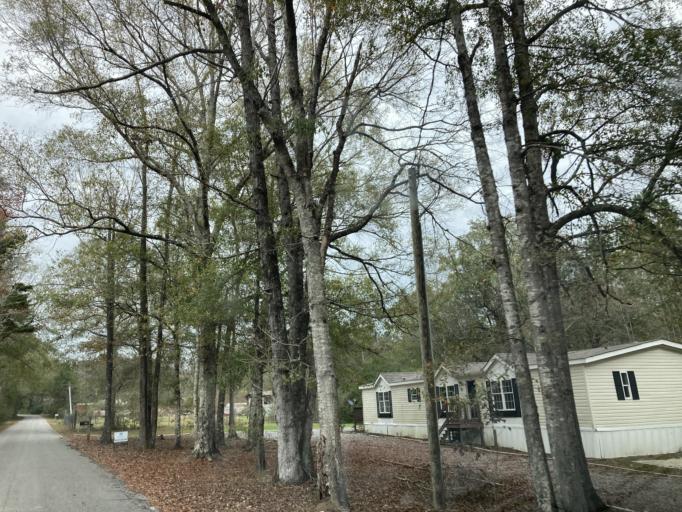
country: US
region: Mississippi
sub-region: Stone County
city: Wiggins
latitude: 31.0601
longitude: -89.2052
